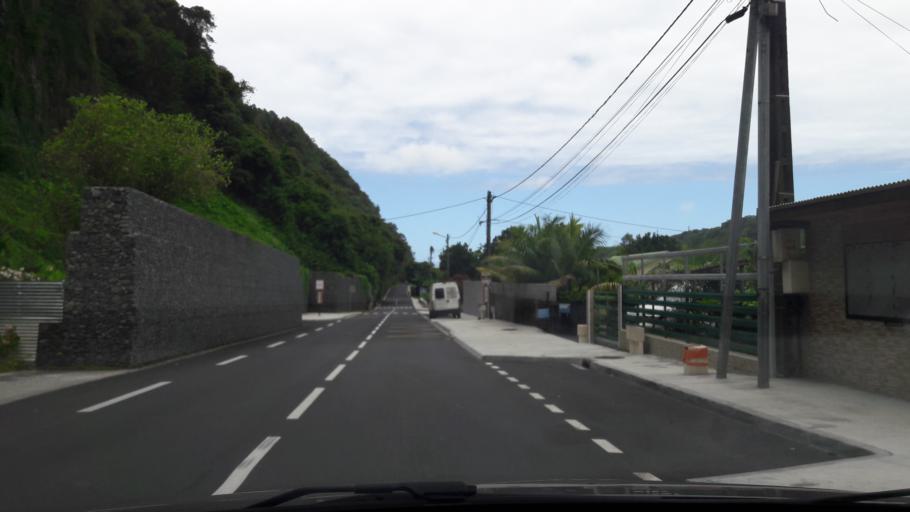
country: RE
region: Reunion
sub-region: Reunion
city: Saint-Andre
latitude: -20.9889
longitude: 55.6163
